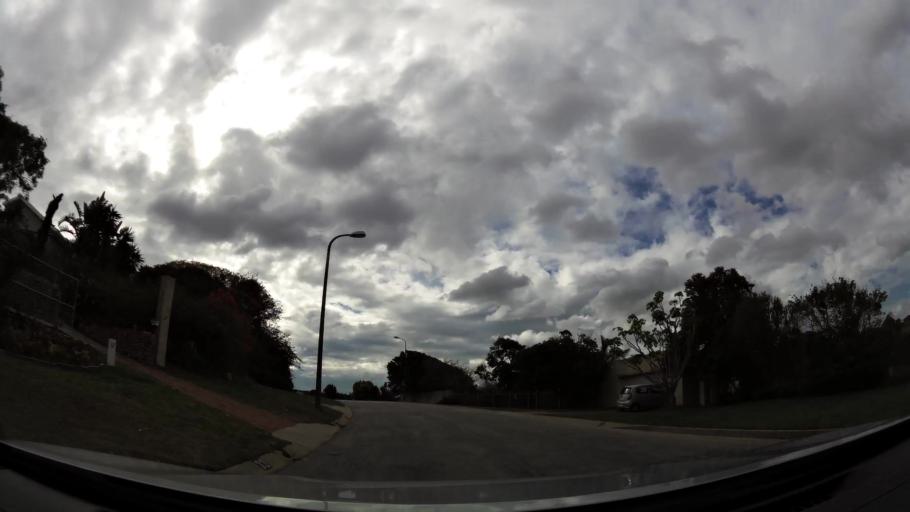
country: ZA
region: Eastern Cape
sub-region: Nelson Mandela Bay Metropolitan Municipality
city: Port Elizabeth
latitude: -33.9341
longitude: 25.5204
